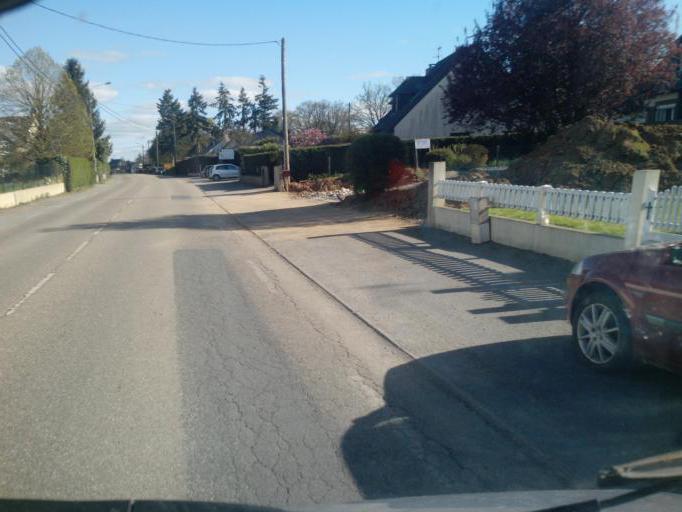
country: FR
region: Brittany
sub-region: Departement d'Ille-et-Vilaine
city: Guipry
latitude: 47.8316
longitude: -1.8487
